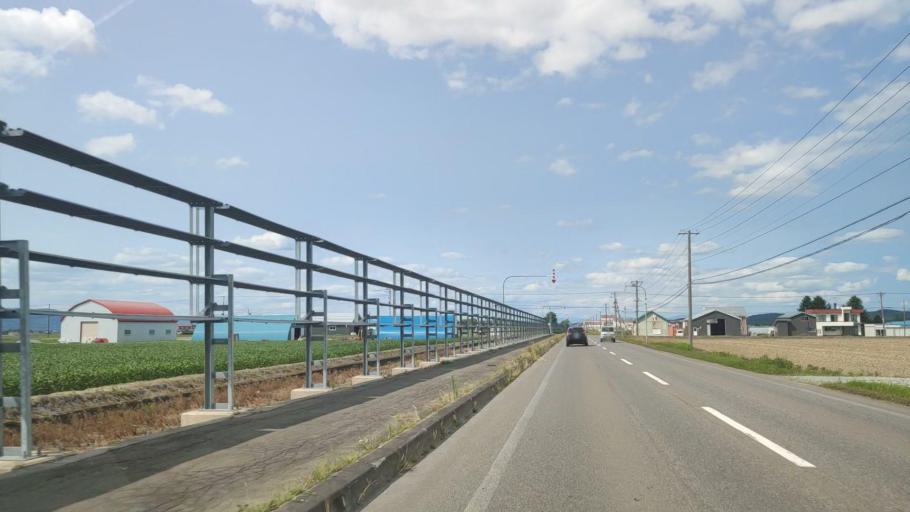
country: JP
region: Hokkaido
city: Nayoro
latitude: 44.1944
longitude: 142.4159
